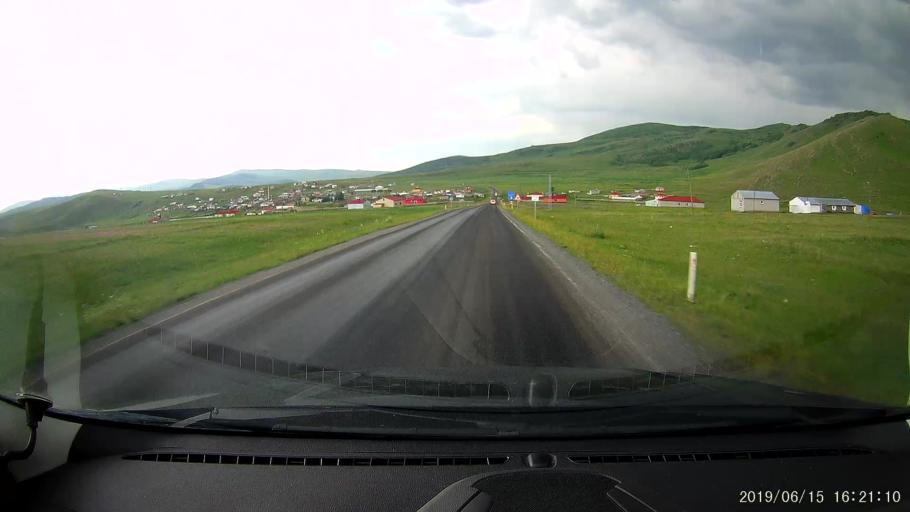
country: TR
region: Ardahan
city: Hanak
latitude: 41.2016
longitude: 42.8461
